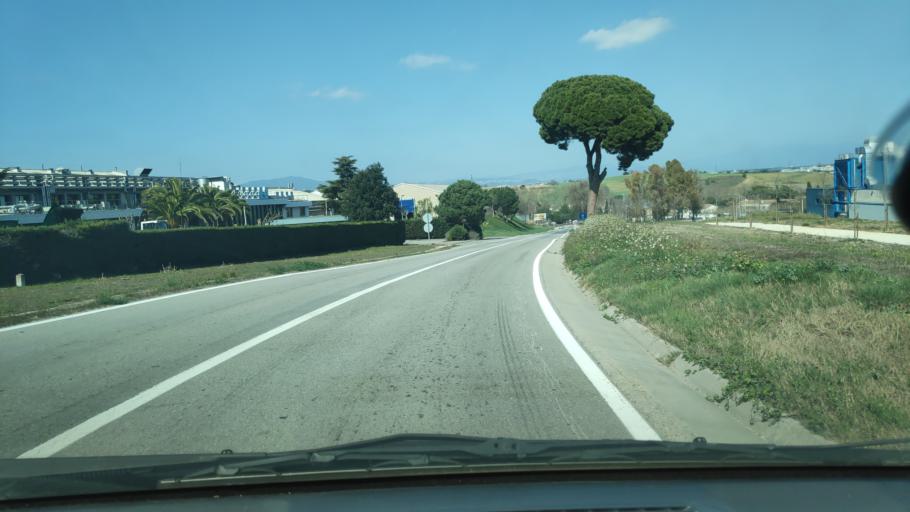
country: ES
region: Catalonia
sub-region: Provincia de Barcelona
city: Polinya
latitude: 41.5297
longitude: 2.1523
